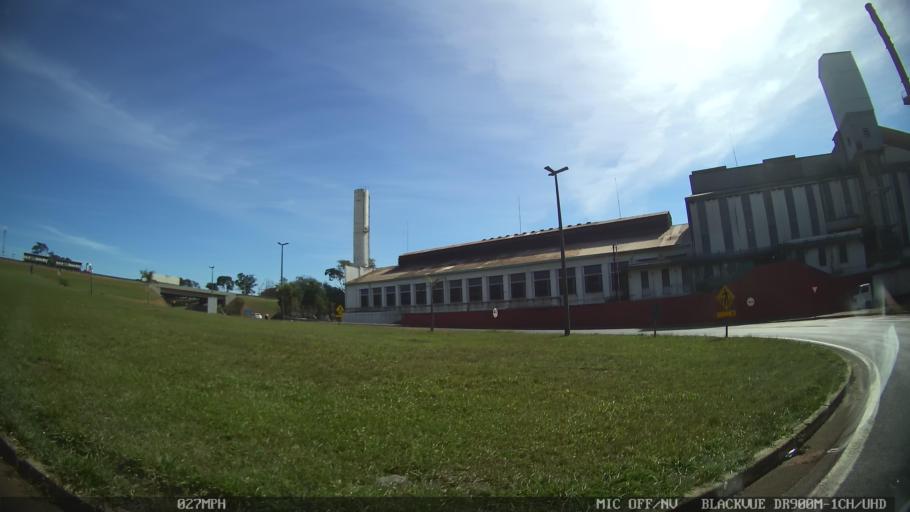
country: BR
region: Sao Paulo
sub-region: Porto Ferreira
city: Porto Ferreira
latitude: -21.8511
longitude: -47.4938
